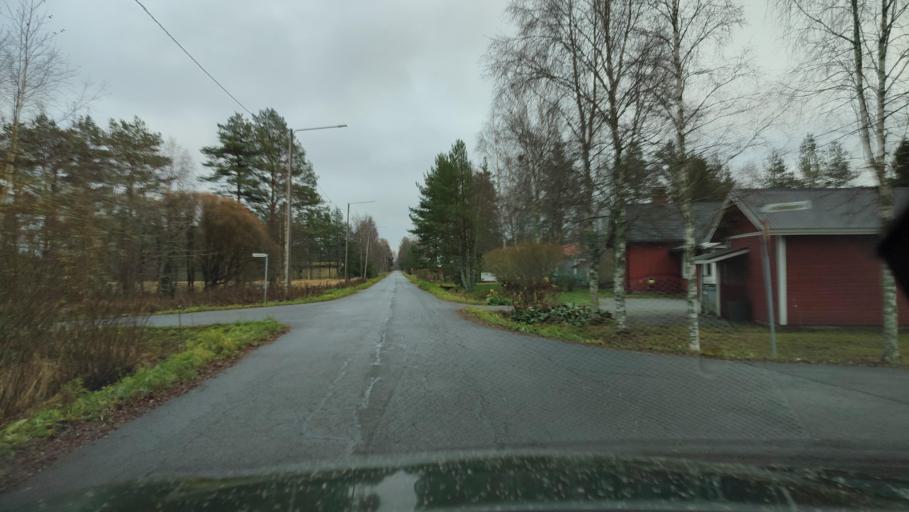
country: FI
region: Southern Ostrobothnia
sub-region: Suupohja
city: Teuva
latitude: 62.4571
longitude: 21.5937
